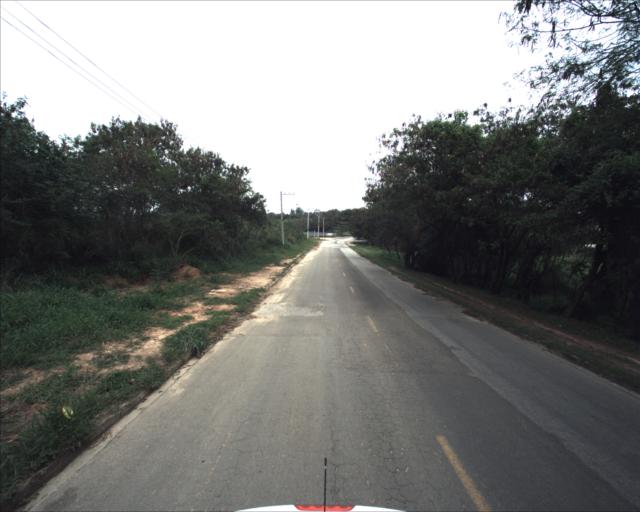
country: BR
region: Sao Paulo
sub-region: Sorocaba
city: Sorocaba
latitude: -23.4519
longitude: -47.3793
